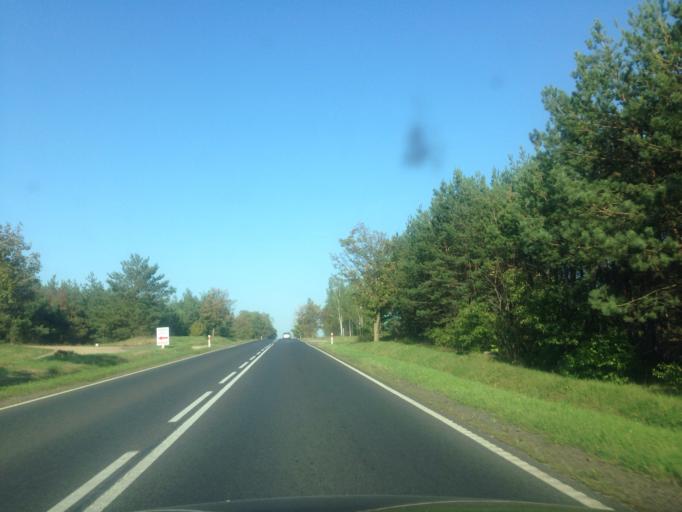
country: PL
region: Kujawsko-Pomorskie
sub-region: Powiat brodnicki
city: Brzozie
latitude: 53.3163
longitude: 19.5265
